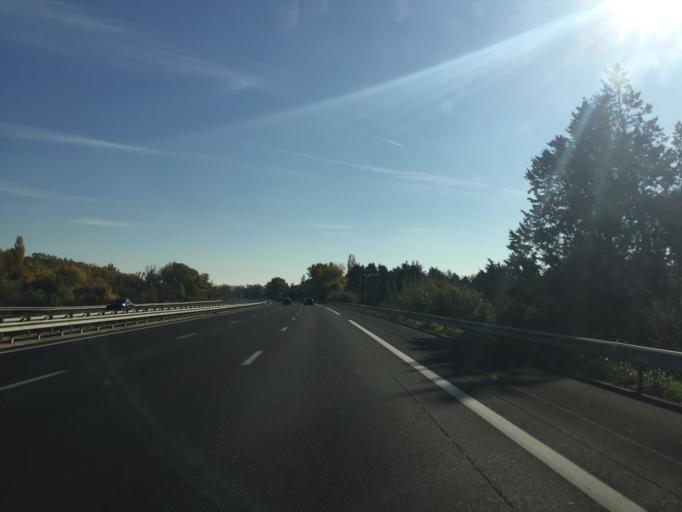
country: FR
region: Provence-Alpes-Cote d'Azur
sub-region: Departement des Bouches-du-Rhone
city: Cabannes
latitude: 43.8444
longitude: 4.9913
